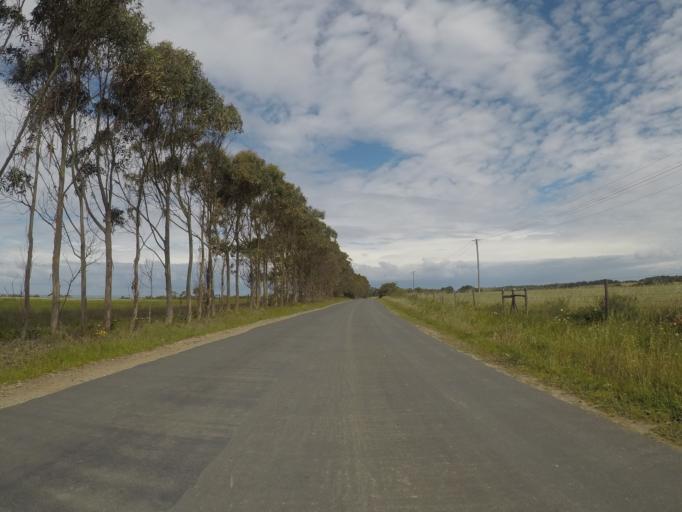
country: PT
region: Beja
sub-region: Odemira
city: Sao Teotonio
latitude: 37.4911
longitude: -8.7813
